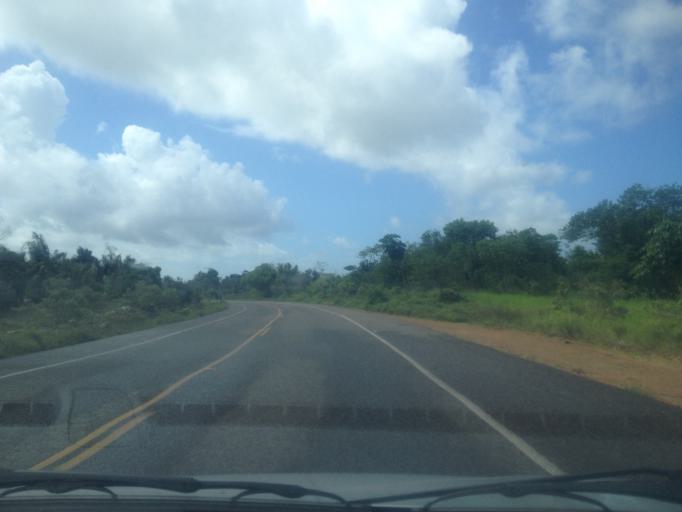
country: BR
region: Bahia
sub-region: Conde
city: Conde
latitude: -12.0830
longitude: -37.7662
